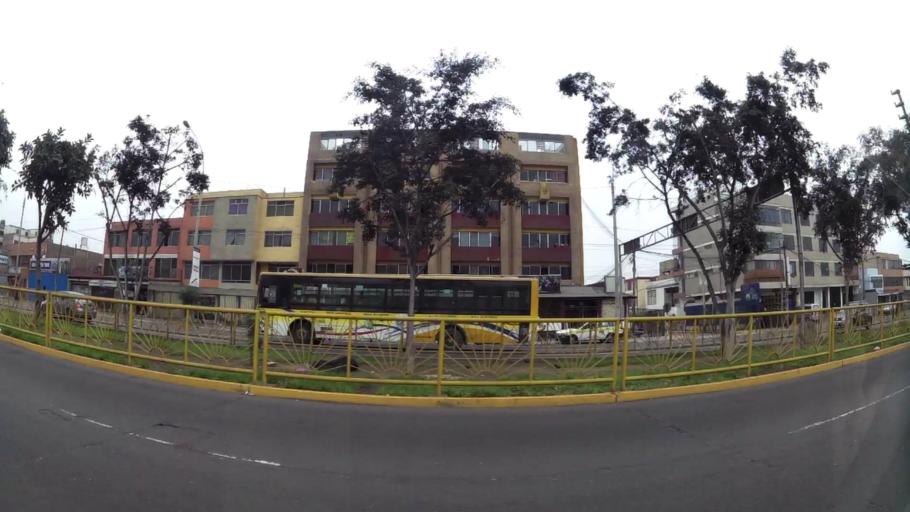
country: PE
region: Lima
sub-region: Lima
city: San Luis
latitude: -12.0816
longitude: -77.0184
